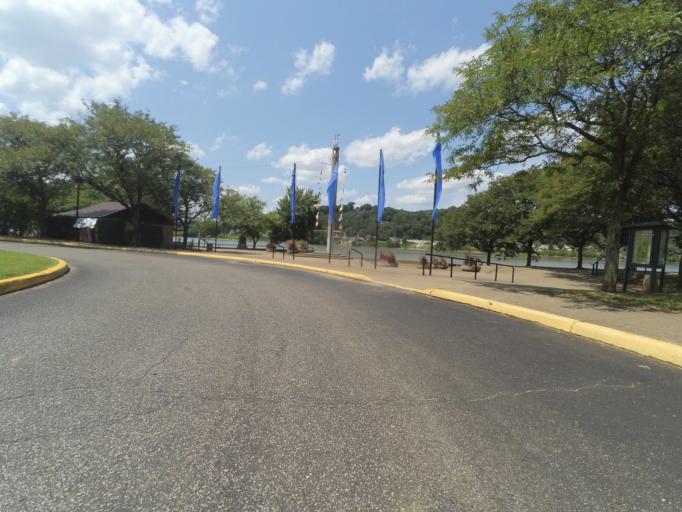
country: US
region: West Virginia
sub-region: Cabell County
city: Huntington
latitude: 38.4240
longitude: -82.4429
